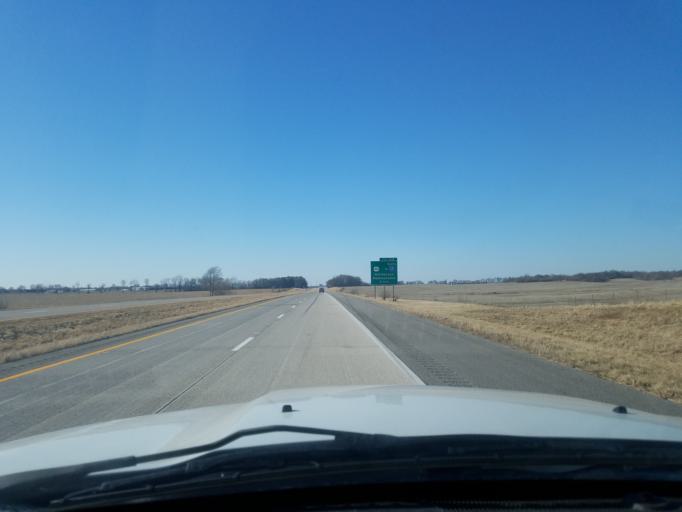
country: US
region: Kentucky
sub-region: Henderson County
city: Henderson
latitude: 37.8039
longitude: -87.5243
